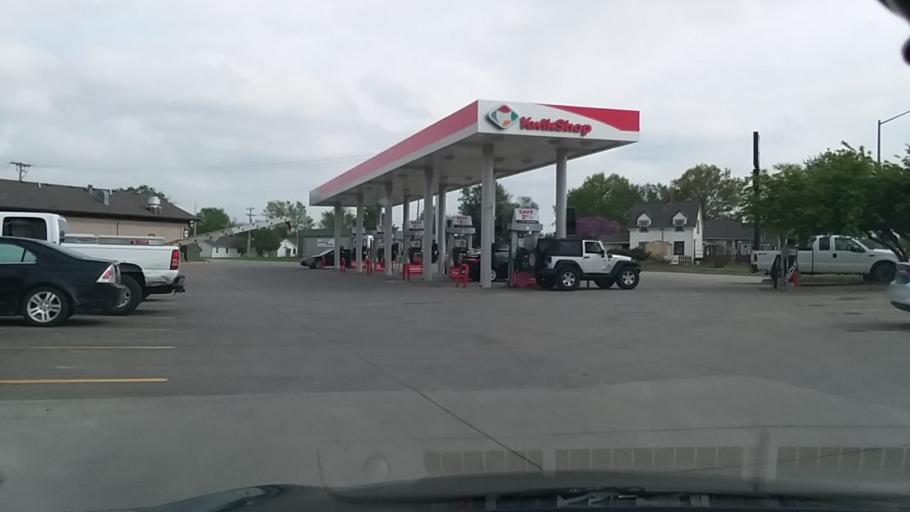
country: US
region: Kansas
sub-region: Douglas County
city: Baldwin City
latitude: 38.7829
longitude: -95.1861
